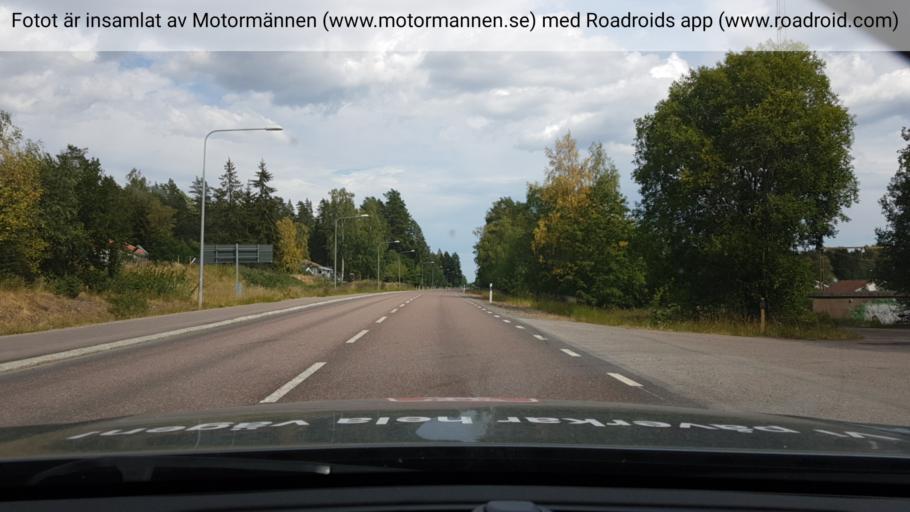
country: SE
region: Uppsala
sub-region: Enkopings Kommun
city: Orsundsbro
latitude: 59.8856
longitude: 17.2017
